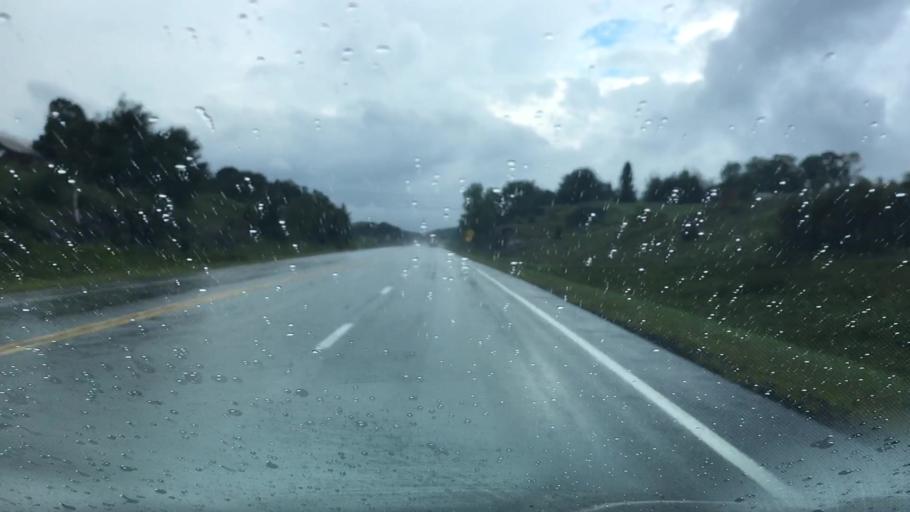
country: US
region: Vermont
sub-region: Caledonia County
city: St Johnsbury
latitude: 44.4339
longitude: -72.0859
